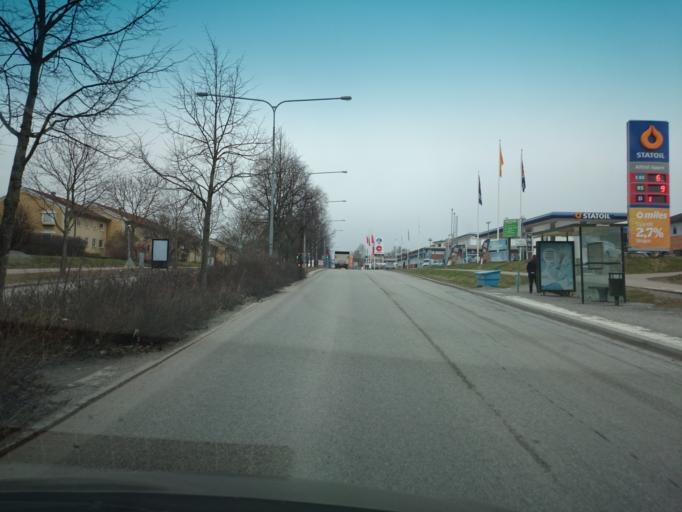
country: SE
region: Uppsala
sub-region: Uppsala Kommun
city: Uppsala
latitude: 59.8665
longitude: 17.6298
